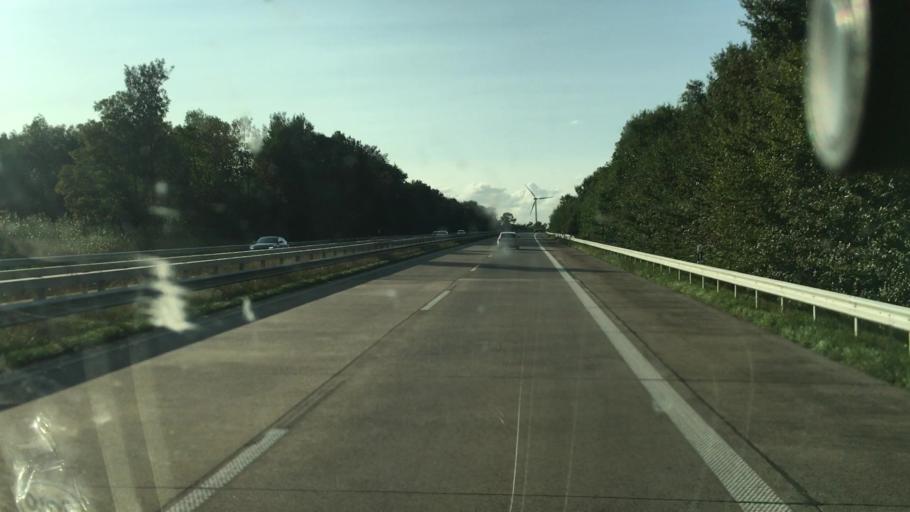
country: DE
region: Lower Saxony
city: Bockhorn
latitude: 53.4316
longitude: 8.0506
